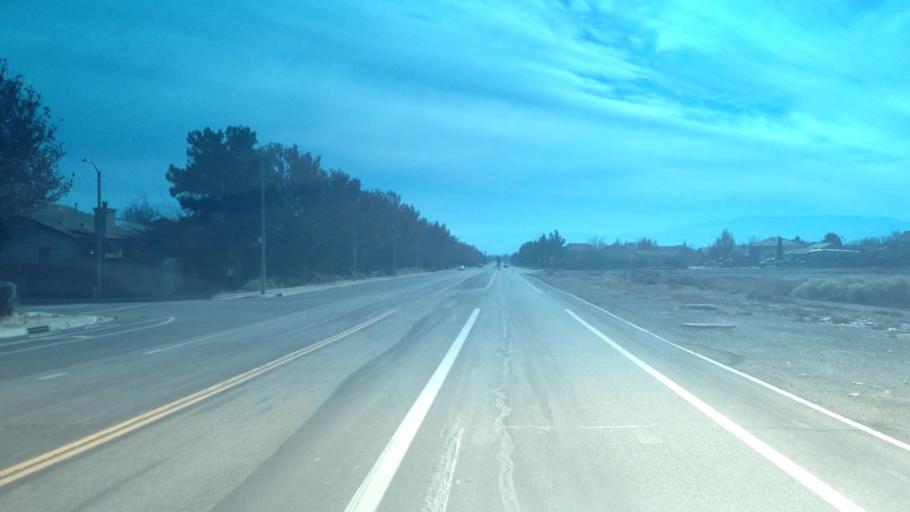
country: US
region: California
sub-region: Los Angeles County
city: Lancaster
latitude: 34.7173
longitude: -118.1662
